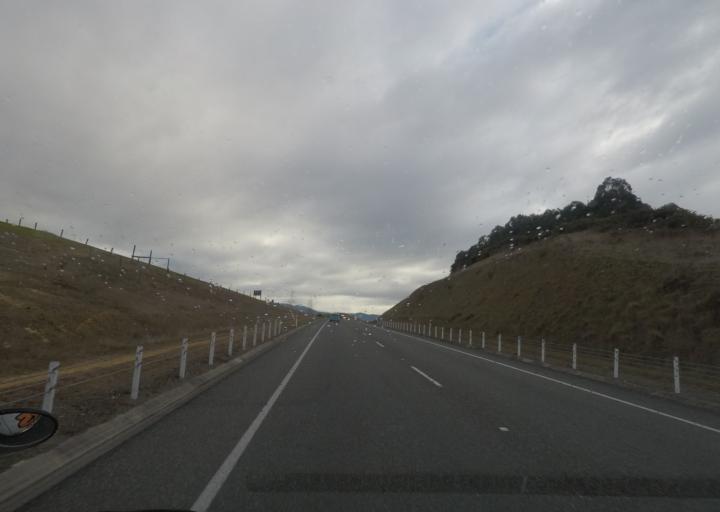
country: NZ
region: Tasman
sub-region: Tasman District
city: Mapua
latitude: -41.2385
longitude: 173.0528
